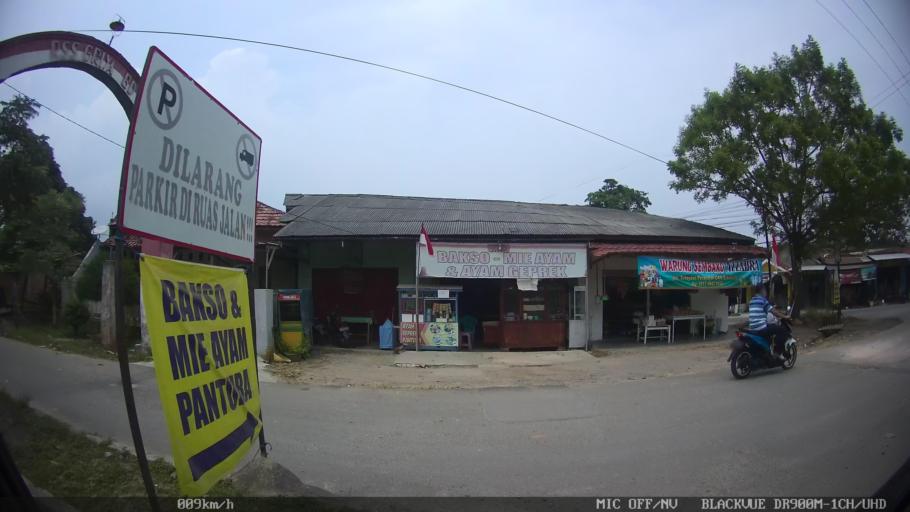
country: ID
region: Lampung
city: Kedaton
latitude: -5.4042
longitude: 105.3182
